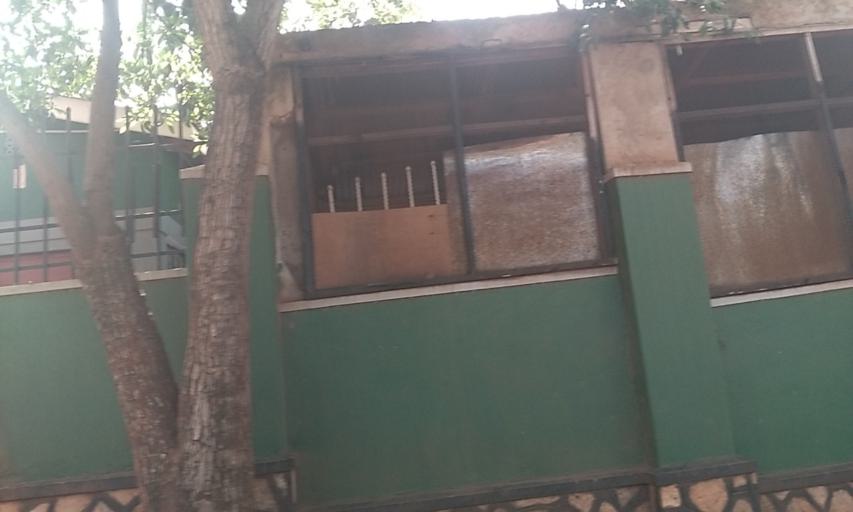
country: UG
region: Central Region
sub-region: Wakiso District
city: Kireka
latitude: 0.3482
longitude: 32.6153
